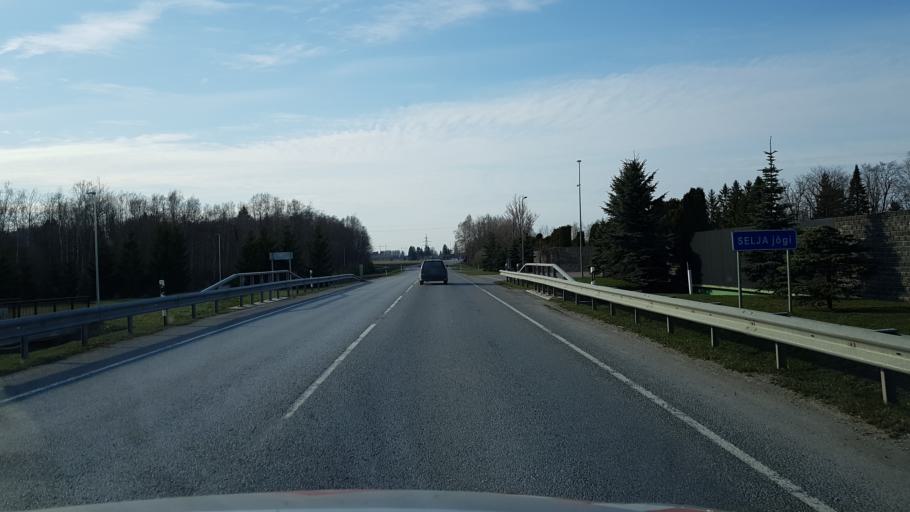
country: EE
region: Laeaene-Virumaa
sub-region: Rakvere linn
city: Rakvere
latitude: 59.3798
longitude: 26.3232
